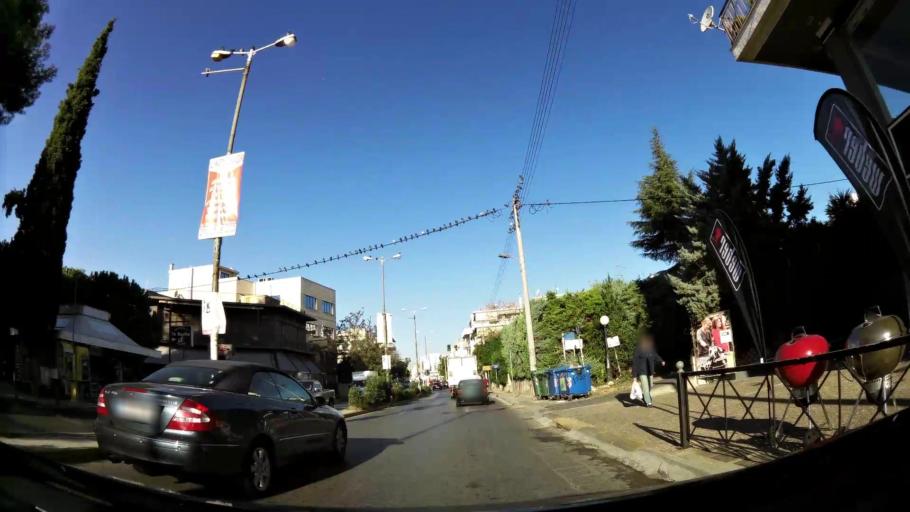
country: GR
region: Attica
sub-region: Nomarchia Athinas
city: Marousi
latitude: 38.0533
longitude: 23.8141
